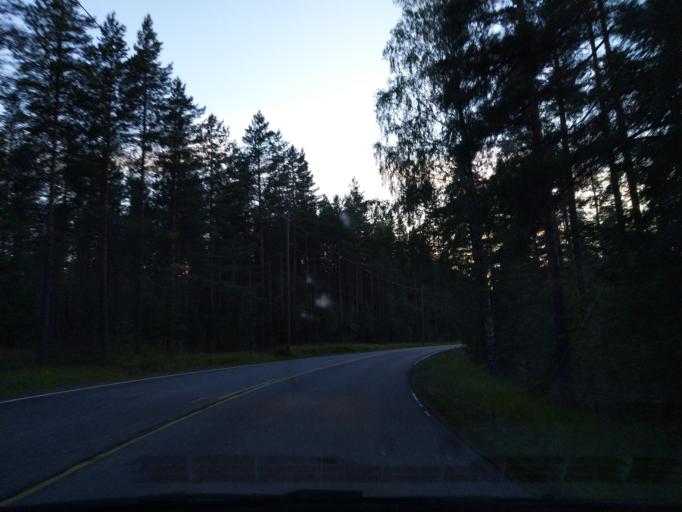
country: FI
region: Uusimaa
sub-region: Helsinki
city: Tuusula
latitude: 60.3524
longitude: 25.0208
